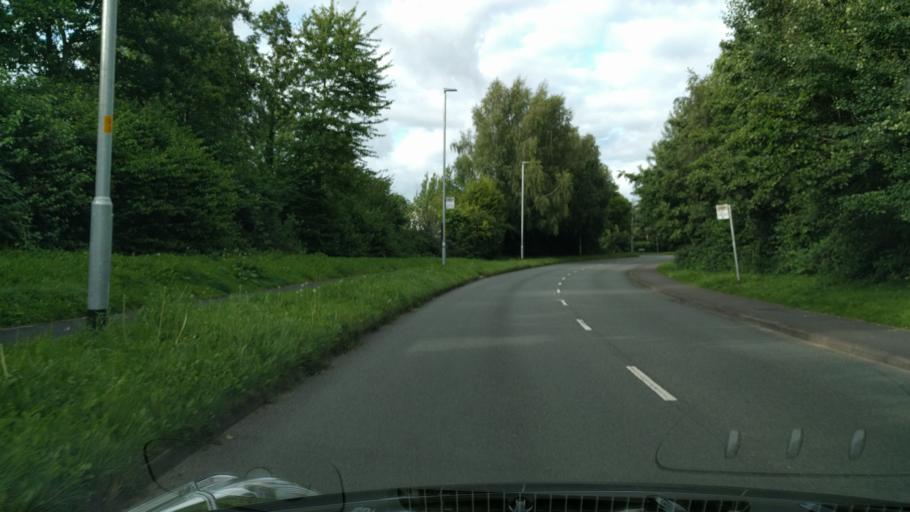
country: GB
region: England
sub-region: Warrington
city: Croft
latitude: 53.4209
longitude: -2.5640
